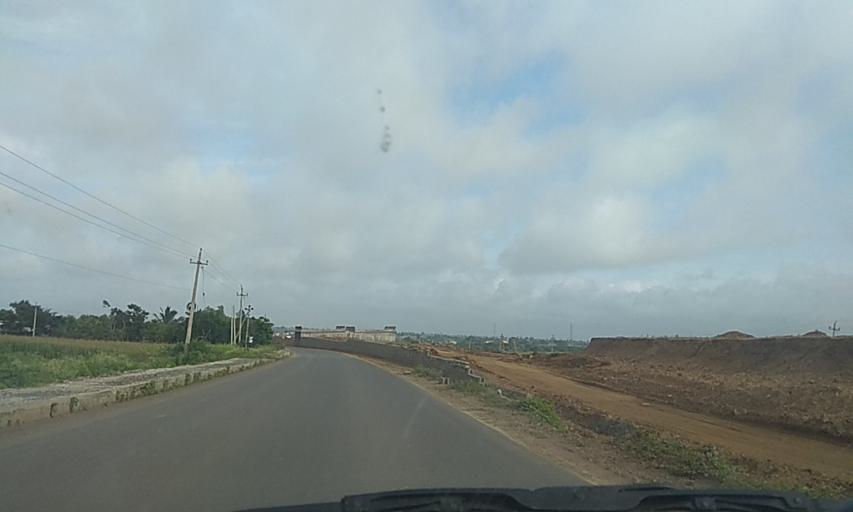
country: IN
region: Karnataka
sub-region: Haveri
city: Haveri
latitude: 14.8528
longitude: 75.3293
